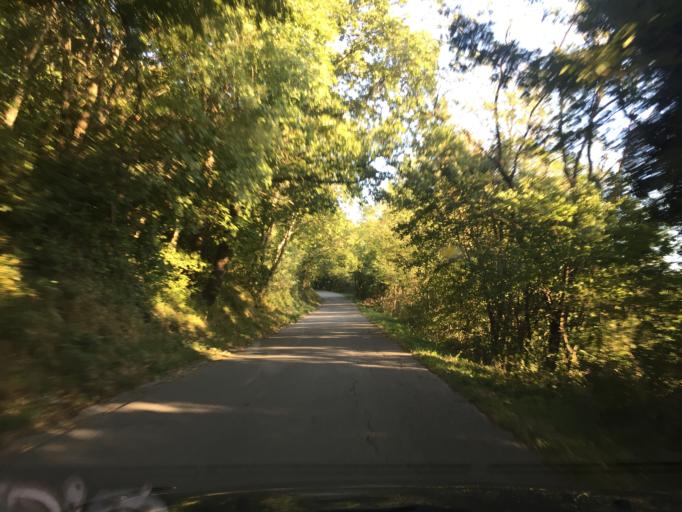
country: SI
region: Vipava
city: Vipava
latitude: 45.7943
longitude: 13.9991
